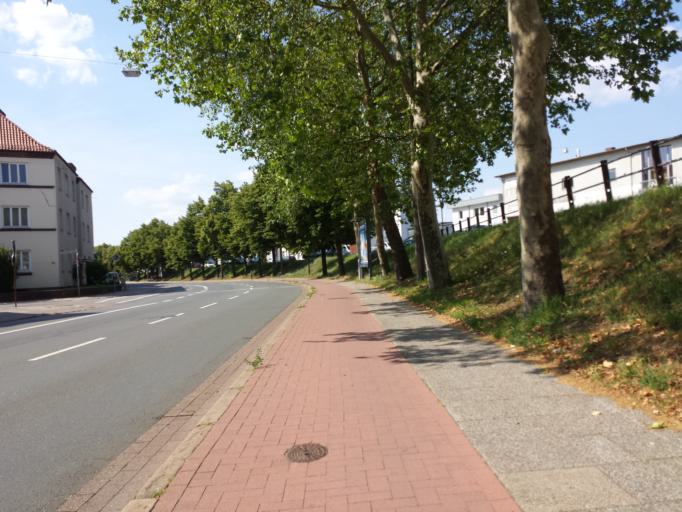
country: DE
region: Bremen
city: Bremen
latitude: 53.0775
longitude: 8.7820
